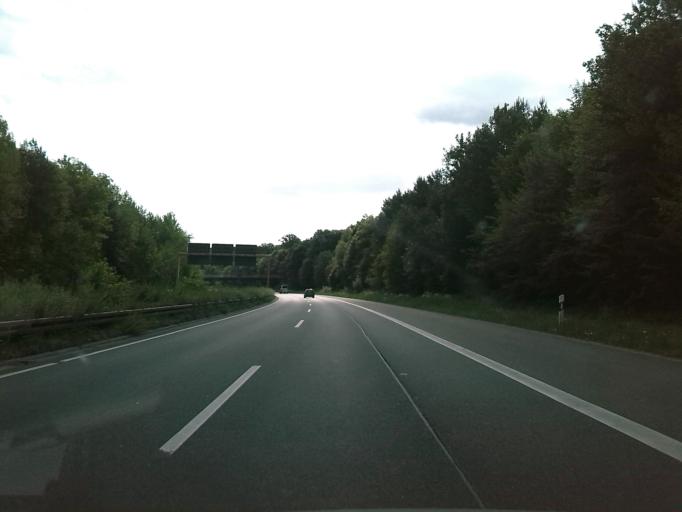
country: DE
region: Hesse
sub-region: Regierungsbezirk Darmstadt
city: Darmstadt
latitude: 49.8658
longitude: 8.6916
